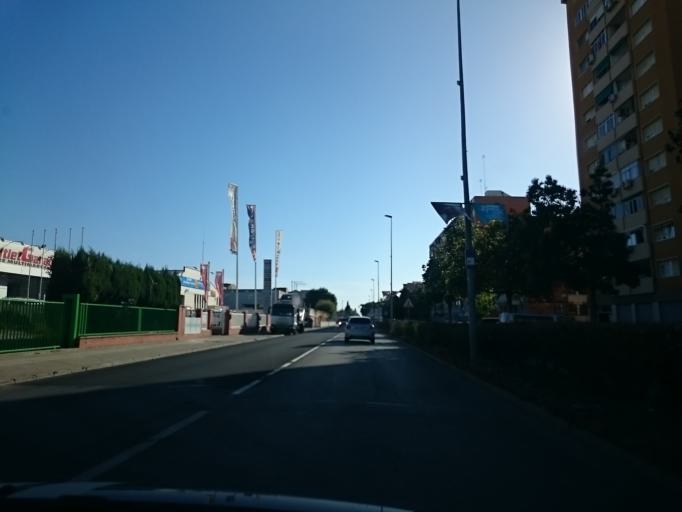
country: ES
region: Catalonia
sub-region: Provincia de Barcelona
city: Viladecans
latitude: 41.3132
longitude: 2.0181
